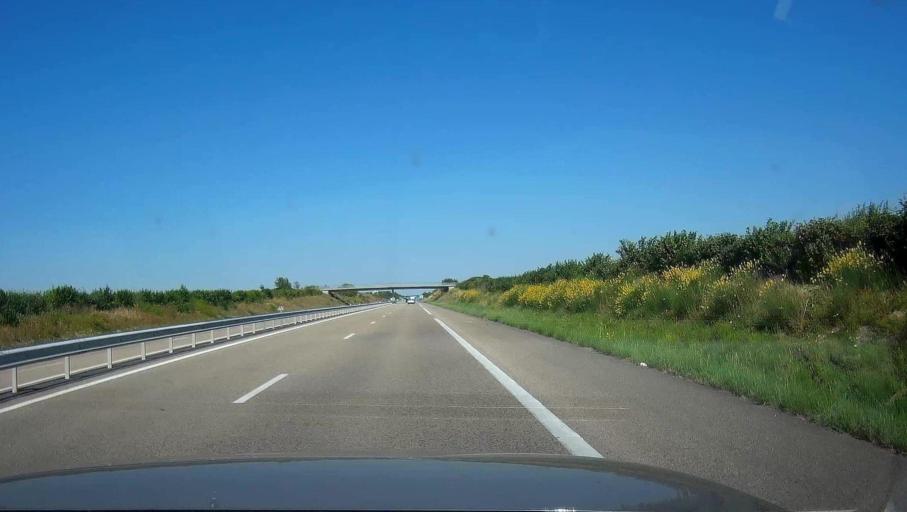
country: FR
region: Champagne-Ardenne
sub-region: Departement de l'Aube
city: Creney-pres-Troyes
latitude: 48.3953
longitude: 4.1521
